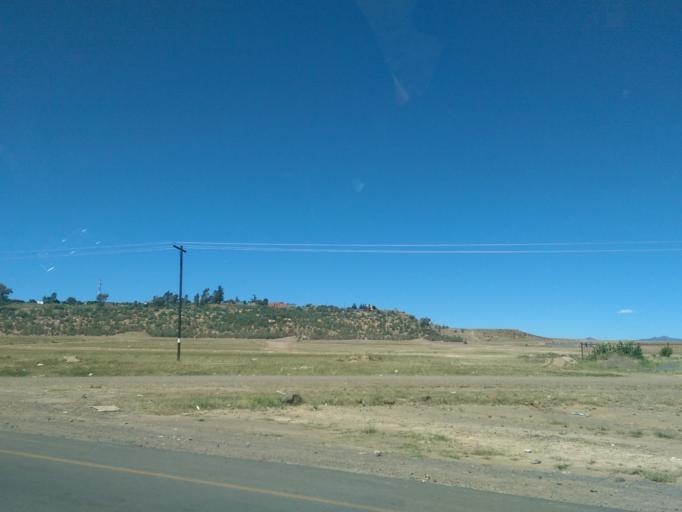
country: LS
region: Maseru
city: Maseru
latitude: -29.3865
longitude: 27.5607
